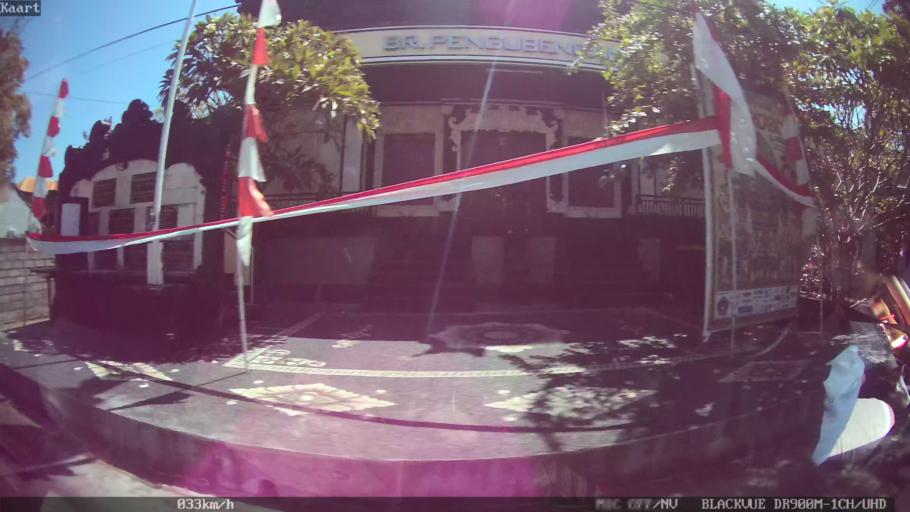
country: ID
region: Bali
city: Denpasar
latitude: -8.6680
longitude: 115.1695
